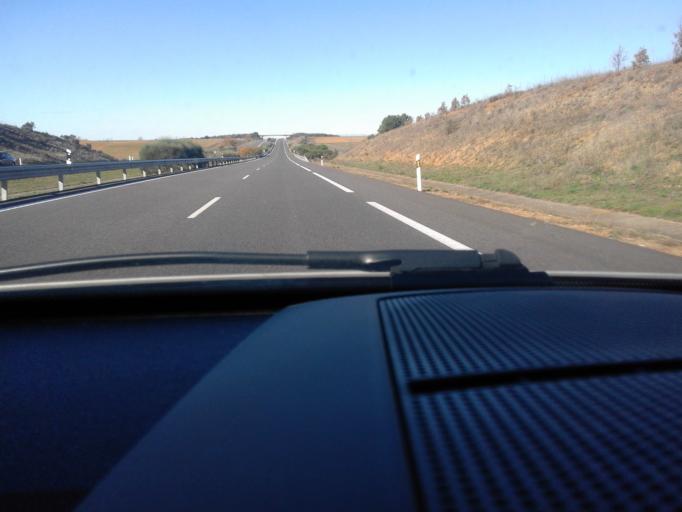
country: ES
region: Castille and Leon
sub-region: Provincia de Leon
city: Villamoratiel de las Matas
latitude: 42.4233
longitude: -5.2875
